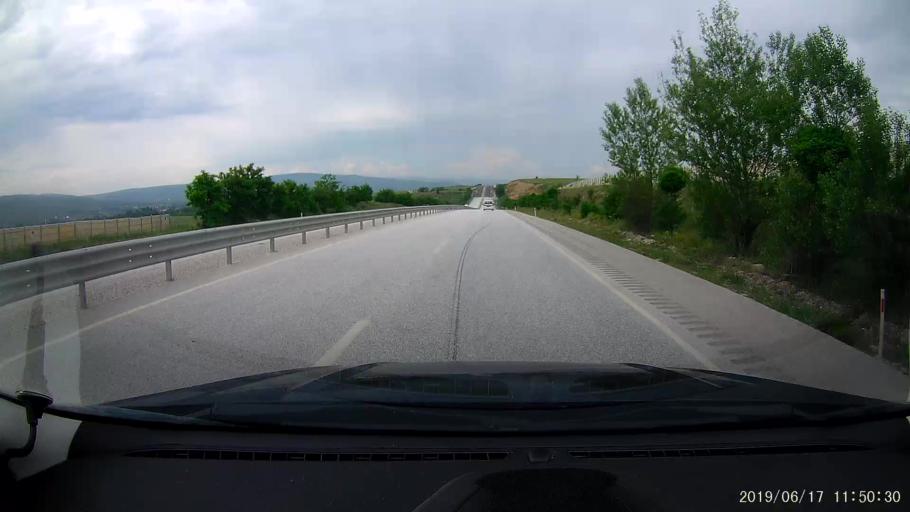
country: TR
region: Cankiri
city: Atkaracalar
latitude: 40.8276
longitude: 33.1300
